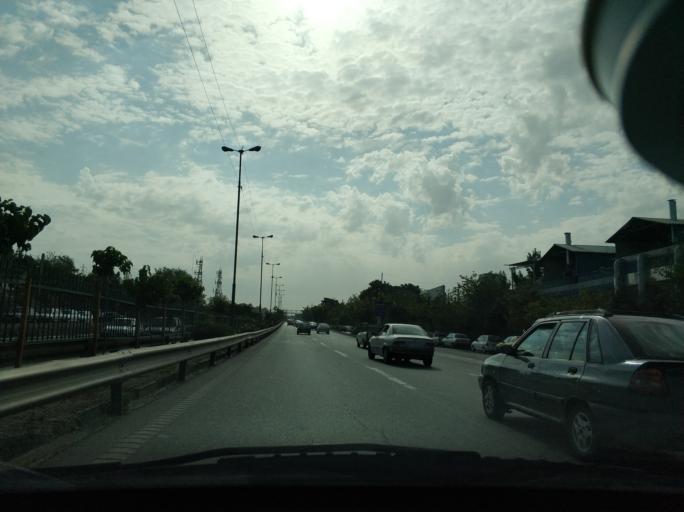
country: IR
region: Tehran
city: Tehran
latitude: 35.7254
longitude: 51.5473
